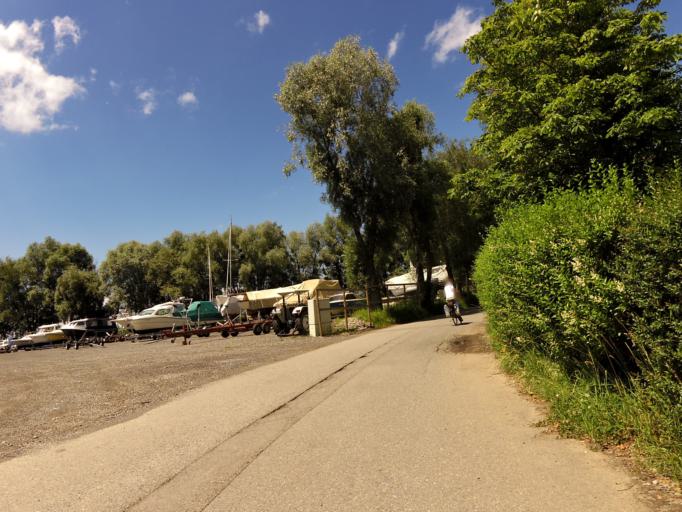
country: AT
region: Vorarlberg
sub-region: Politischer Bezirk Bregenz
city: Fussach
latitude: 47.4884
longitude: 9.6617
